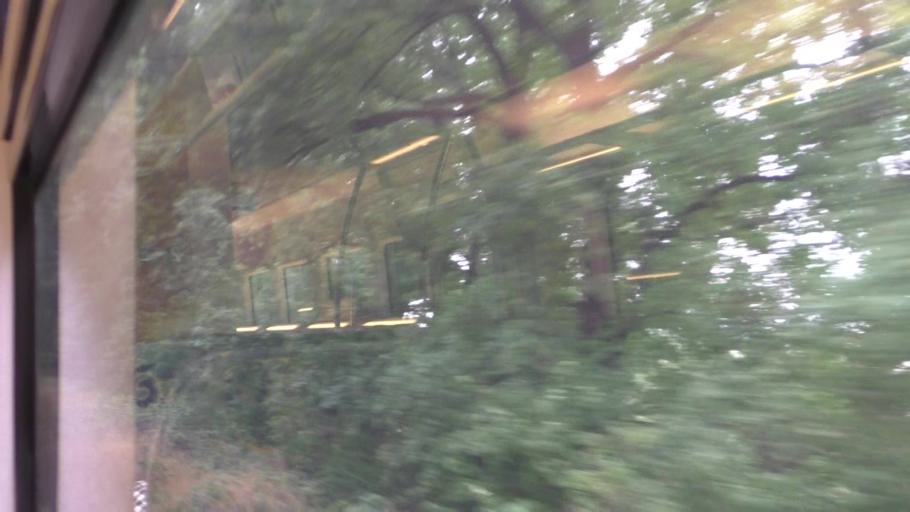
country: DE
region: Saxony
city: Goerlitz
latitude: 51.1735
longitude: 14.9659
